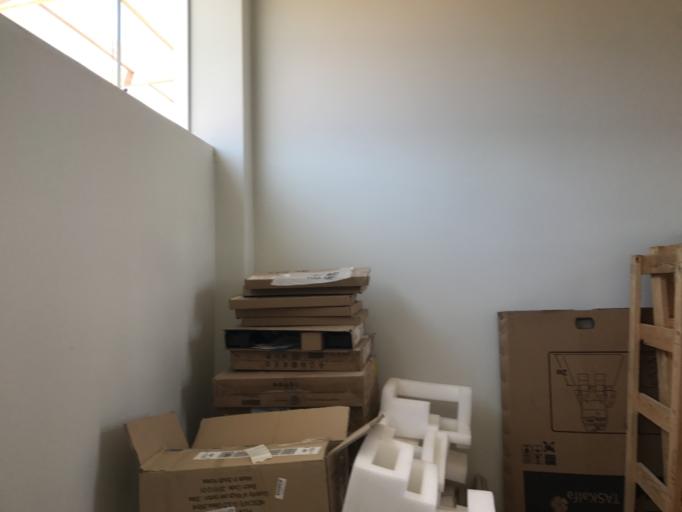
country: PE
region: Arequipa
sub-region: Provincia de Arequipa
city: Arequipa
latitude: -16.3548
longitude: -71.5953
